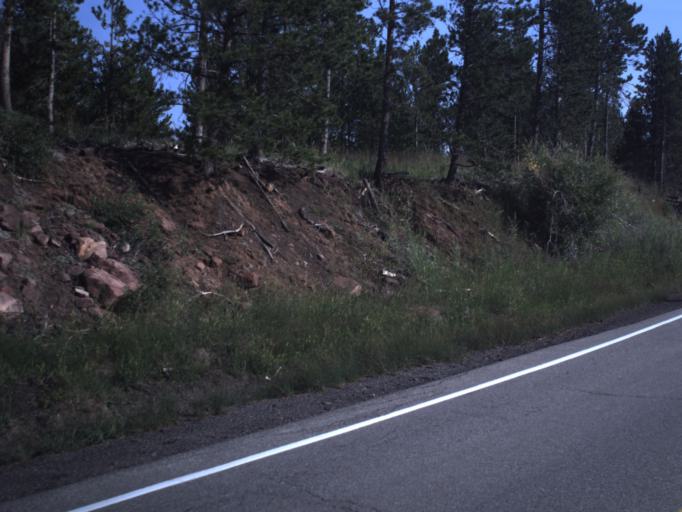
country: US
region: Utah
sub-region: Daggett County
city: Manila
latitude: 40.8328
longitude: -109.4628
